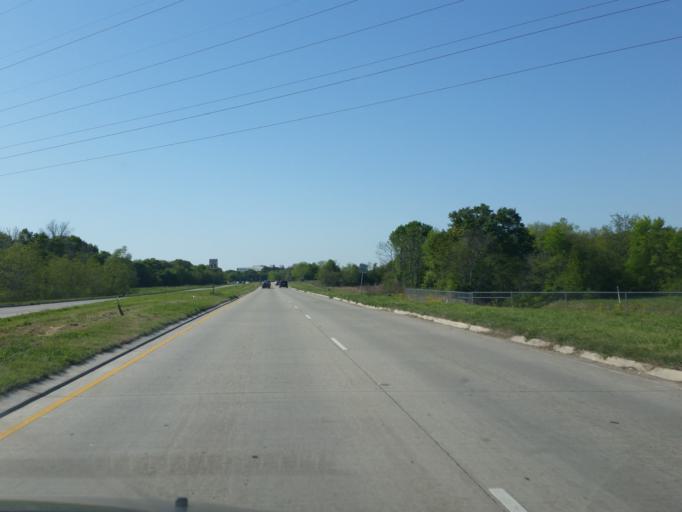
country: US
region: Louisiana
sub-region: Lafayette Parish
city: Youngsville
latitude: 30.1411
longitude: -92.0248
